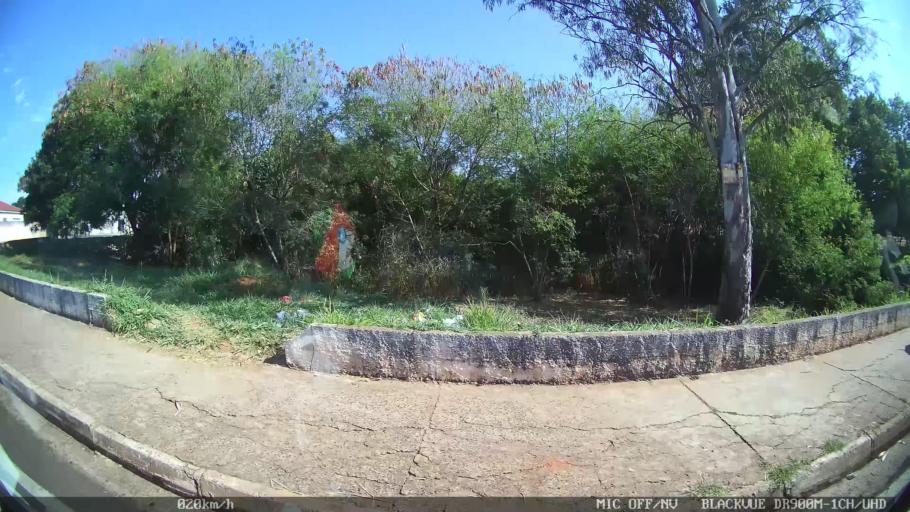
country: BR
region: Sao Paulo
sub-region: Sao Jose Do Rio Preto
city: Sao Jose do Rio Preto
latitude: -20.7783
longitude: -49.3861
